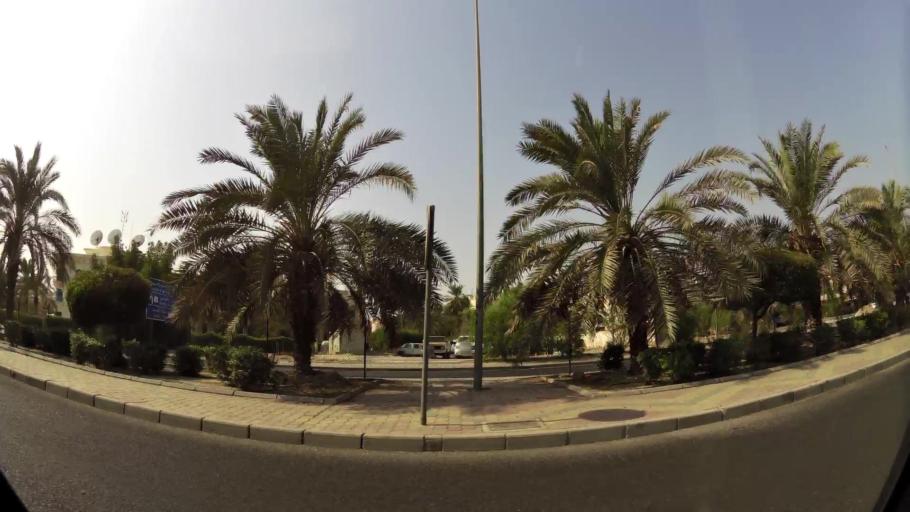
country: KW
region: Al Asimah
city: Ad Dasmah
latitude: 29.3516
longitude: 48.0146
